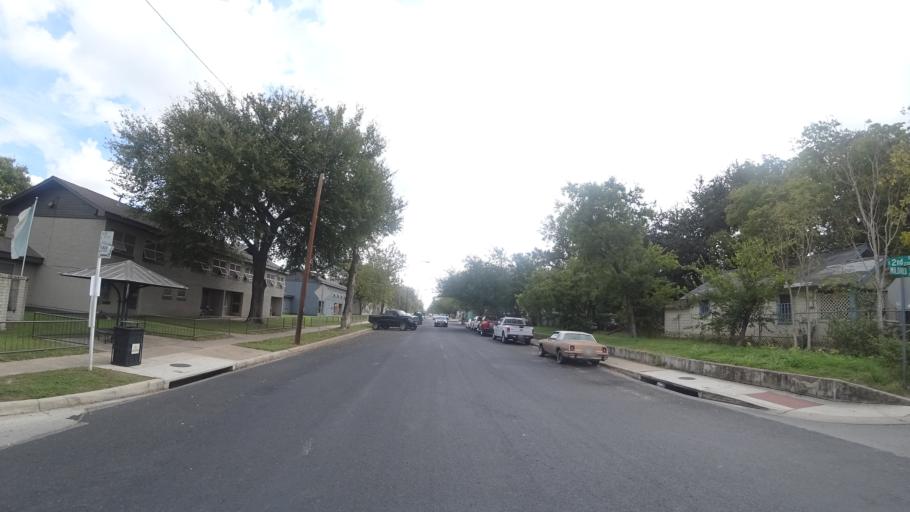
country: US
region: Texas
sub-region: Travis County
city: Austin
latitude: 30.2562
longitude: -97.7188
